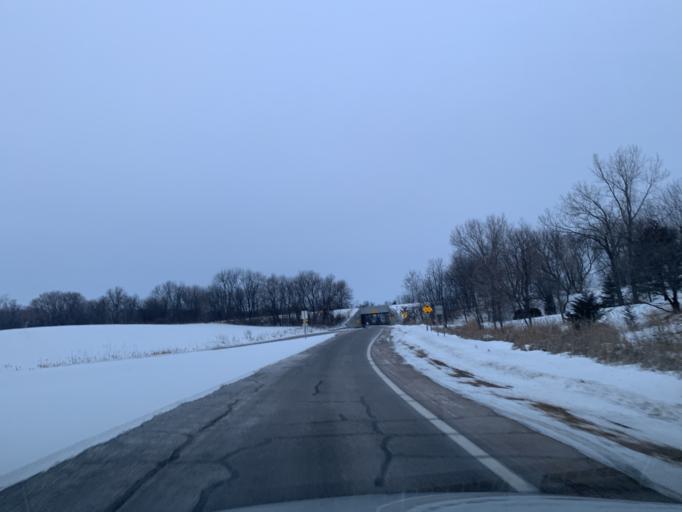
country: US
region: Minnesota
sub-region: Carver County
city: Cologne
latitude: 44.7751
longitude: -93.7545
